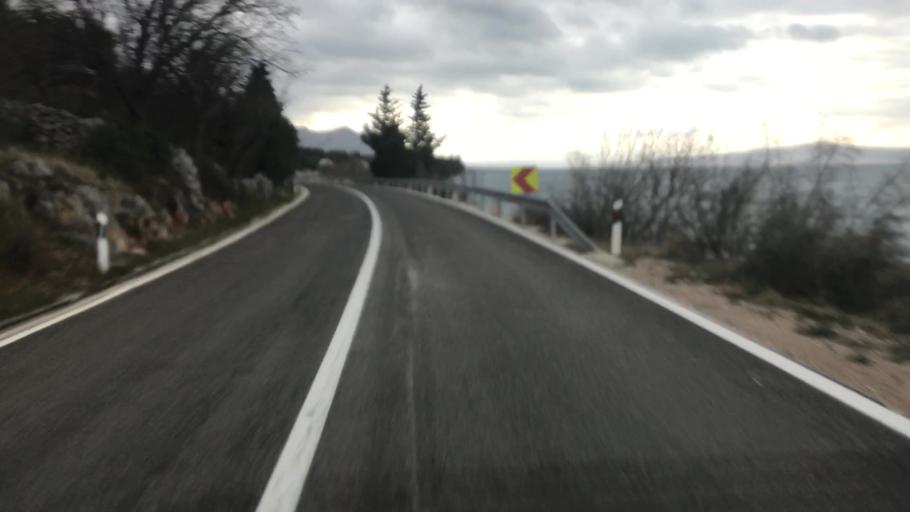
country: HR
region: Zadarska
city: Razanac
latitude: 44.3345
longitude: 15.3529
